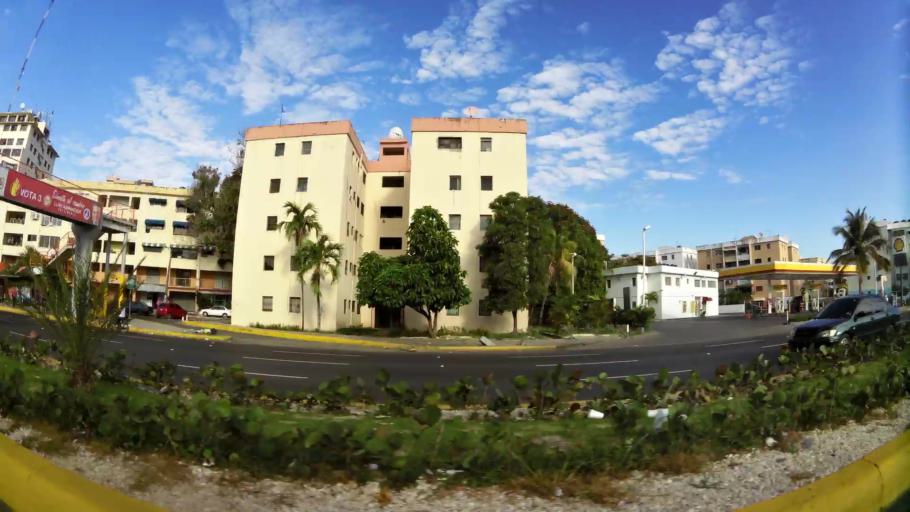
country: DO
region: Nacional
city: San Carlos
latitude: 18.4837
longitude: -69.9048
